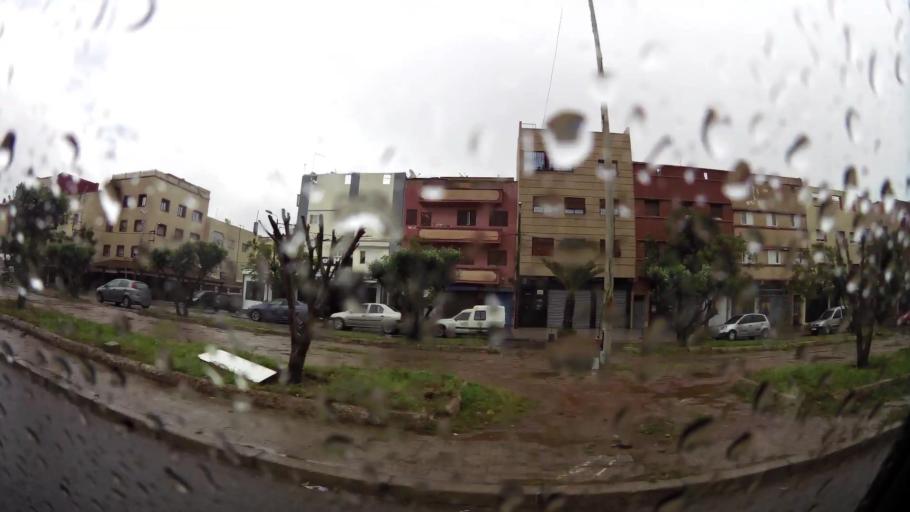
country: MA
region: Grand Casablanca
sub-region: Casablanca
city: Casablanca
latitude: 33.5509
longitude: -7.6792
